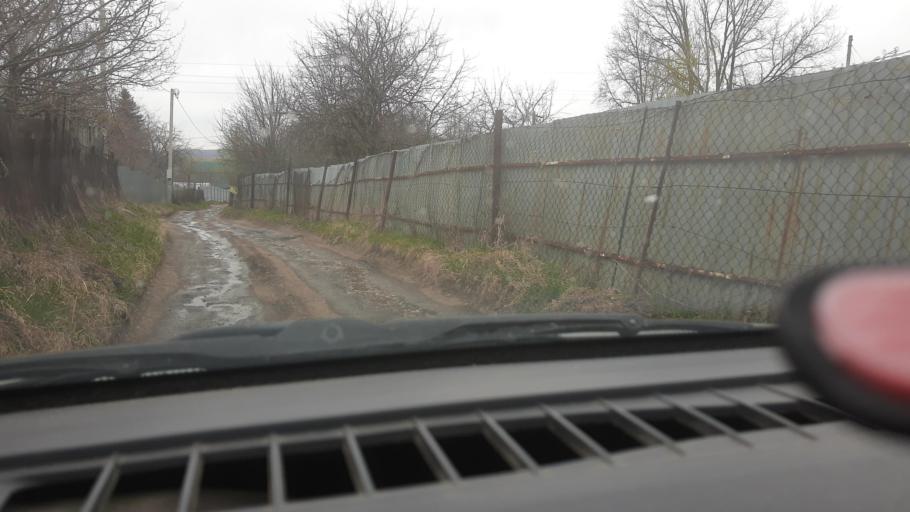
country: RU
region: Bashkortostan
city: Mikhaylovka
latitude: 54.9221
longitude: 55.8838
